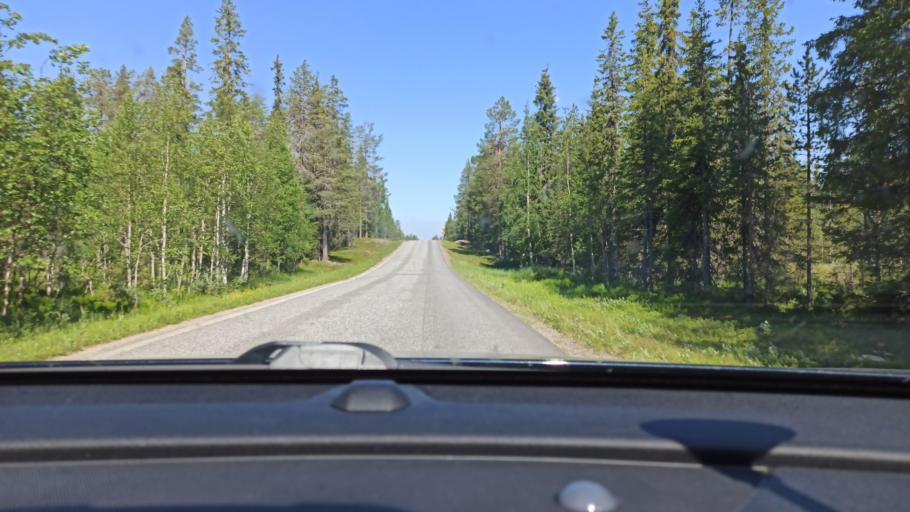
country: FI
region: Lapland
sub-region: Tunturi-Lappi
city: Kolari
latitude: 67.6743
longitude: 24.1456
